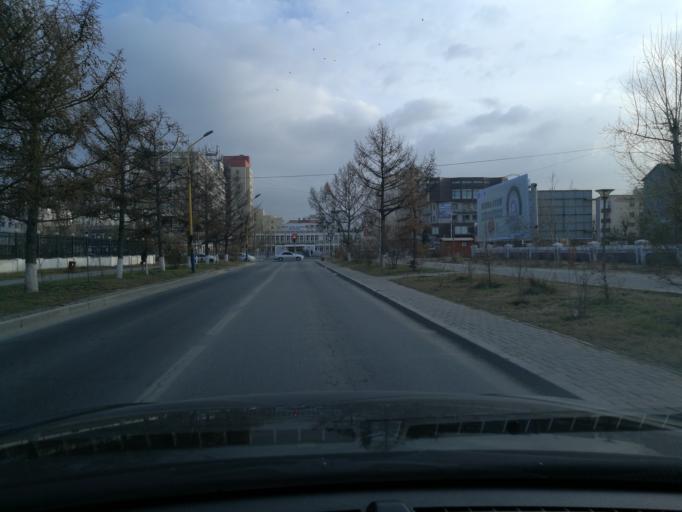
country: MN
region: Ulaanbaatar
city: Ulaanbaatar
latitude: 47.9239
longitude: 106.9276
